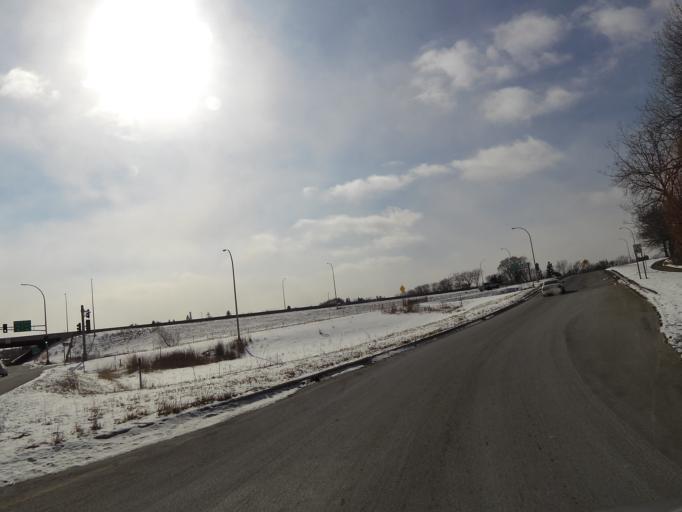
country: US
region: Minnesota
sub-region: Ramsey County
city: Maplewood
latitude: 44.9498
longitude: -92.9864
